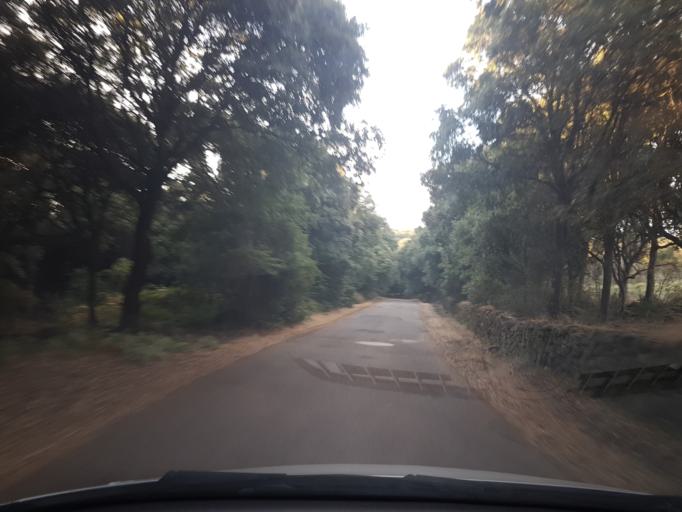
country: IT
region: Sardinia
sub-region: Provincia di Oristano
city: Seneghe
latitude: 40.1109
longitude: 8.5849
